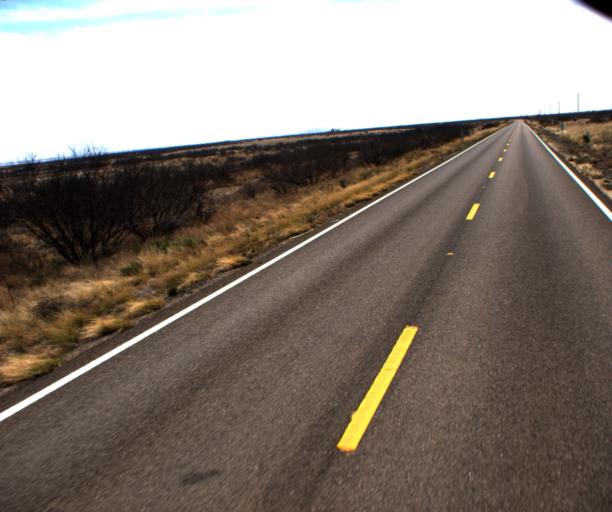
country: US
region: Arizona
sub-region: Cochise County
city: Willcox
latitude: 32.1525
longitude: -109.9373
